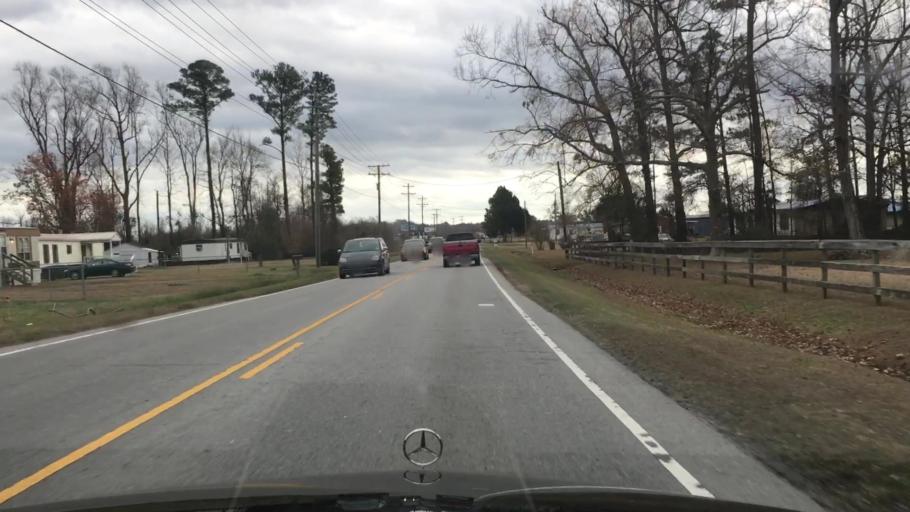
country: US
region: North Carolina
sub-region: Onslow County
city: Half Moon
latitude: 34.8507
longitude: -77.4820
